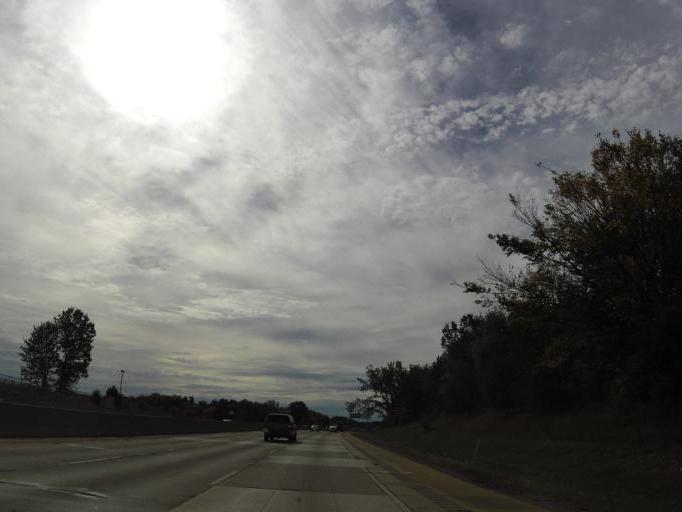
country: US
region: Ohio
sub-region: Summit County
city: Silver Lake
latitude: 41.1911
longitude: -81.4782
